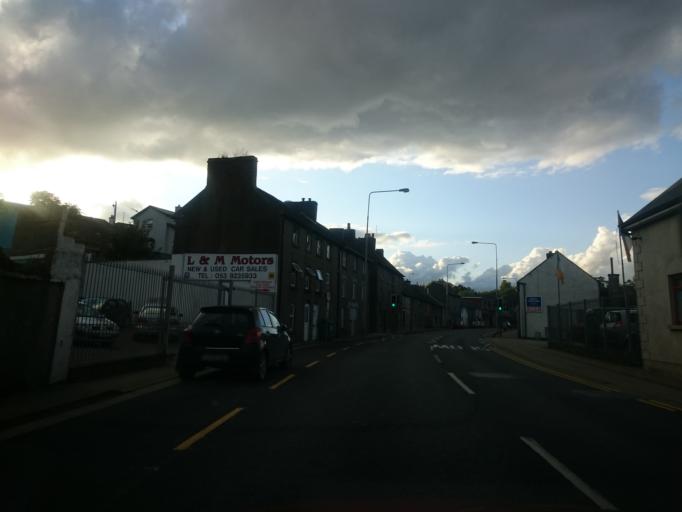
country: IE
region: Leinster
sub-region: Loch Garman
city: Enniscorthy
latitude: 52.5039
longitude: -6.5692
